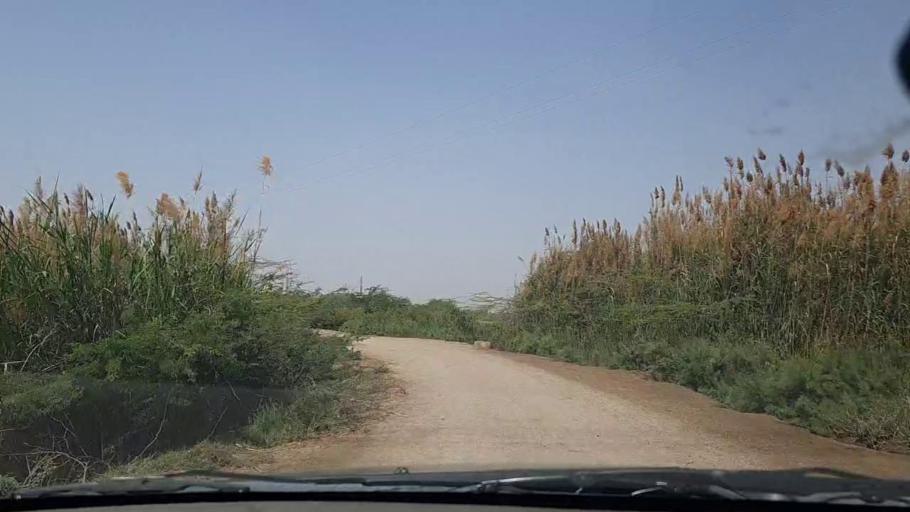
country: PK
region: Sindh
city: Mirpur Sakro
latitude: 24.3216
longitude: 67.6817
